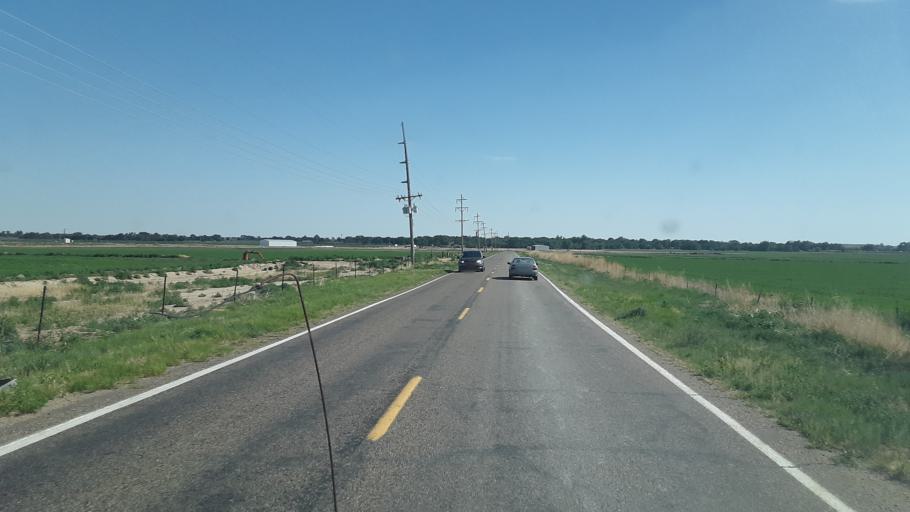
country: US
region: Colorado
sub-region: Crowley County
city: Ordway
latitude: 38.1235
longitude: -103.8628
